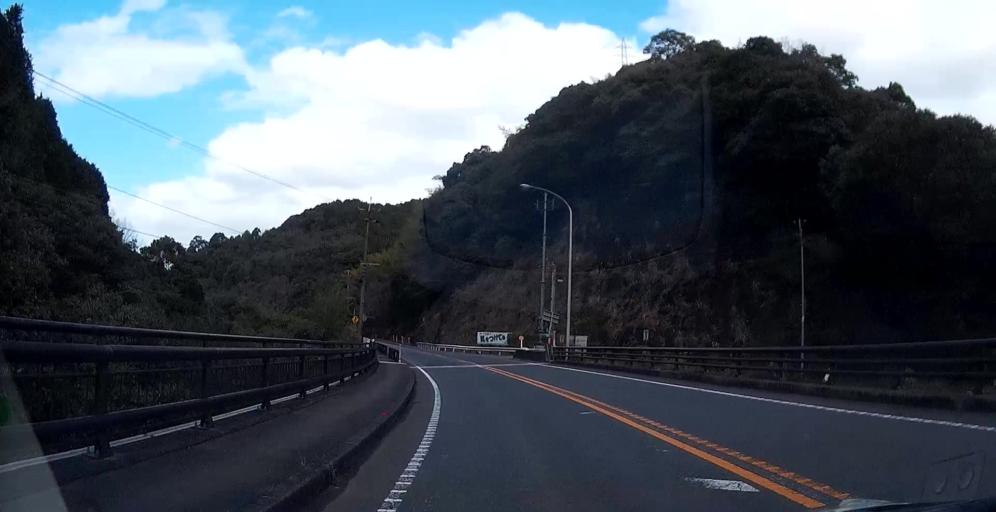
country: JP
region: Kumamoto
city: Yatsushiro
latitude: 32.3753
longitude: 130.5364
